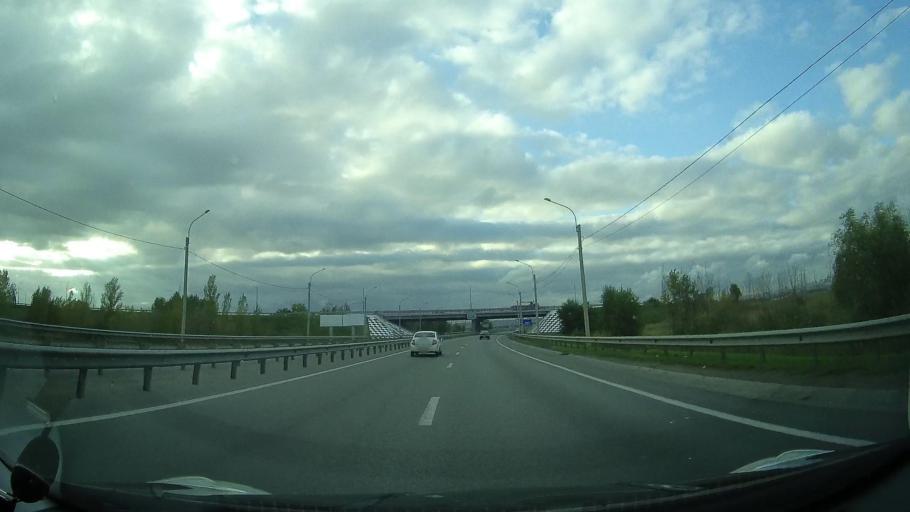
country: RU
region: Rostov
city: Bataysk
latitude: 47.1688
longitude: 39.7492
